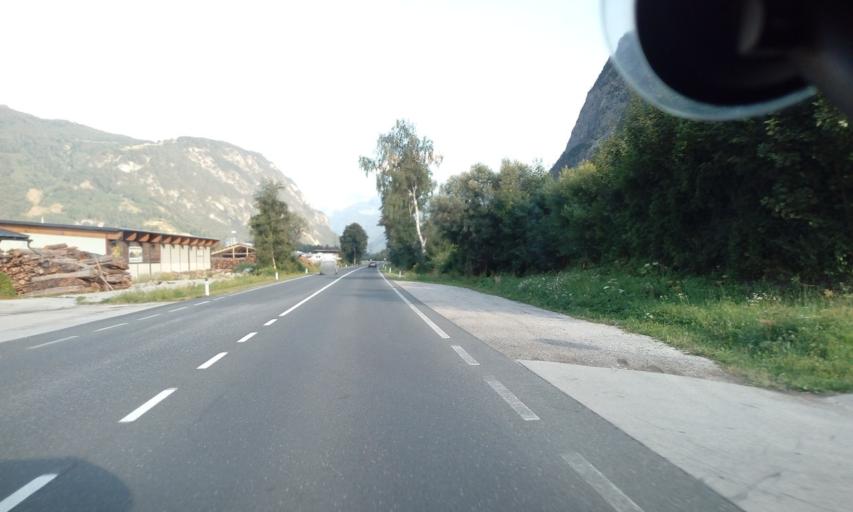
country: AT
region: Tyrol
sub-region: Politischer Bezirk Lienz
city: Nikolsdorf
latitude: 46.7797
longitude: 12.8953
